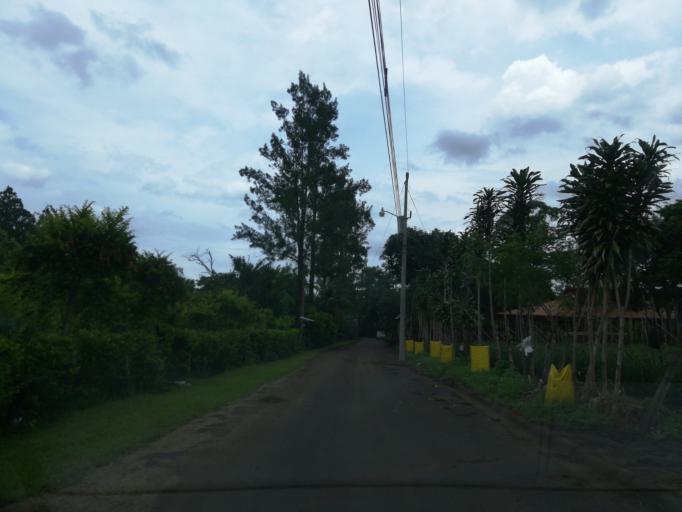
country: CR
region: Alajuela
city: Alajuela
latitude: 10.0331
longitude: -84.1862
